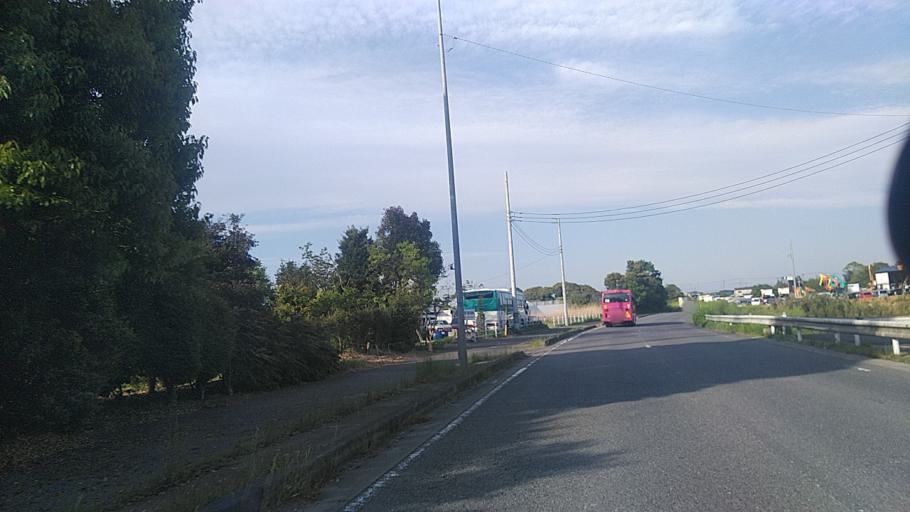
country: JP
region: Chiba
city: Shiroi
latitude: 35.7694
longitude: 140.1085
